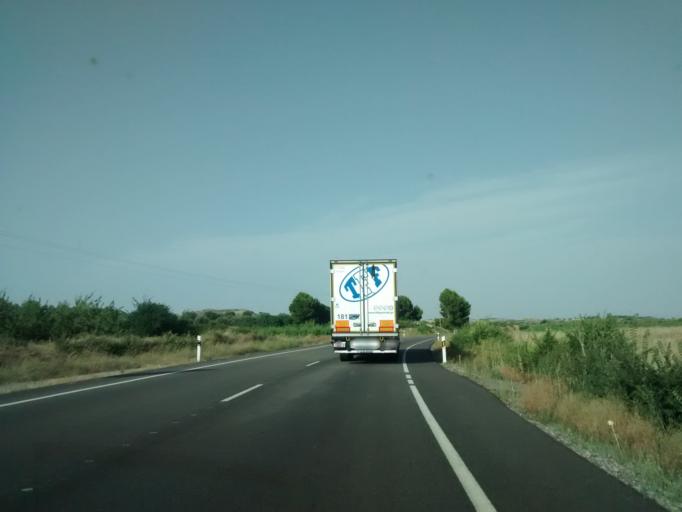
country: ES
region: Aragon
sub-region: Provincia de Zaragoza
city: Bulbuente
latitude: 41.8274
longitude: -1.5820
